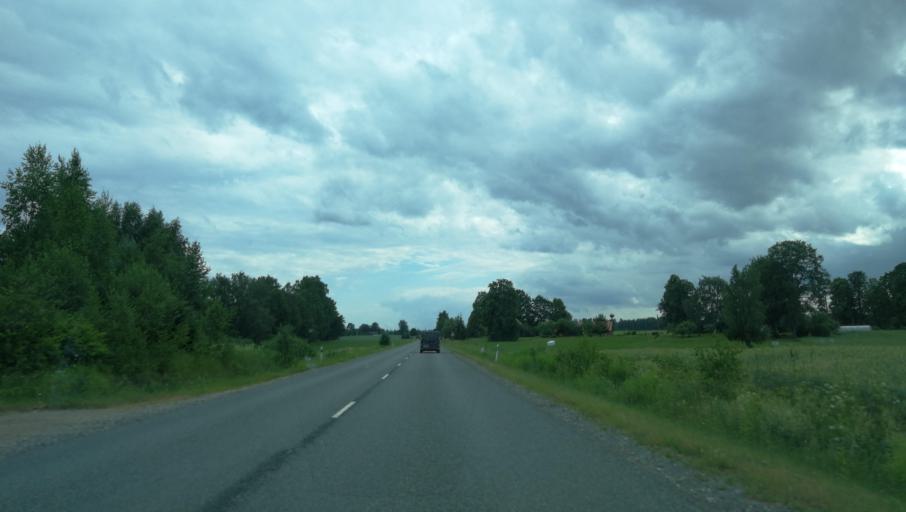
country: LV
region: Naukseni
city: Naukseni
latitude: 57.7418
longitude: 25.4297
